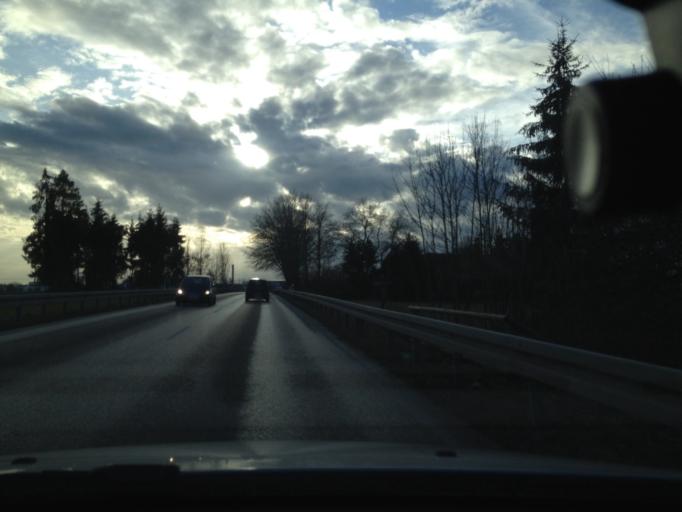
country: DE
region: Bavaria
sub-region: Swabia
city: Schwabmunchen
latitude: 48.2028
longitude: 10.7662
